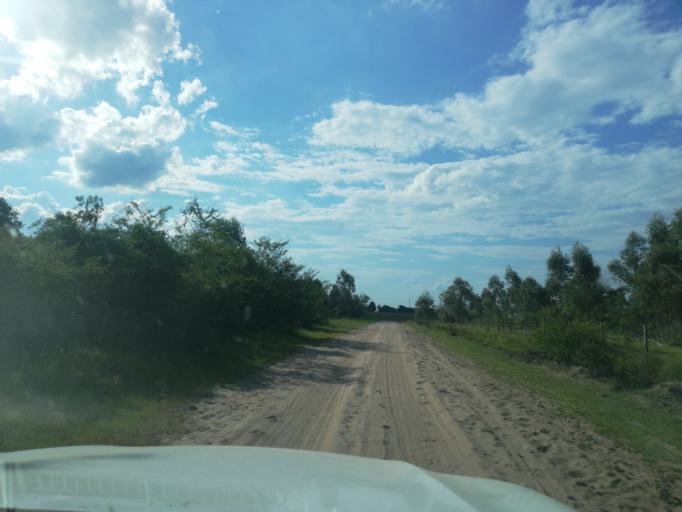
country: AR
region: Corrientes
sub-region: Departamento de San Miguel
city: San Miguel
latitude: -27.9903
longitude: -57.5671
